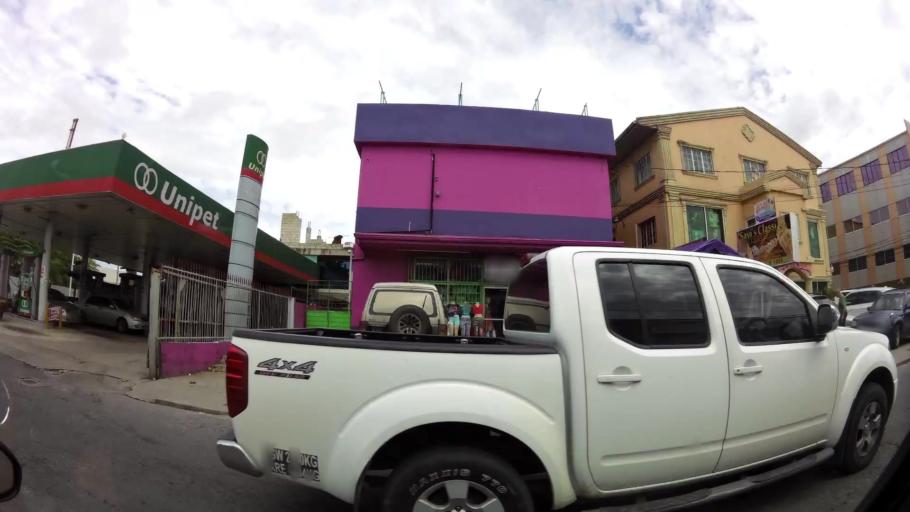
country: TT
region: Couva-Tabaquite-Talparo
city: Couva
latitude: 10.4218
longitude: -61.4590
